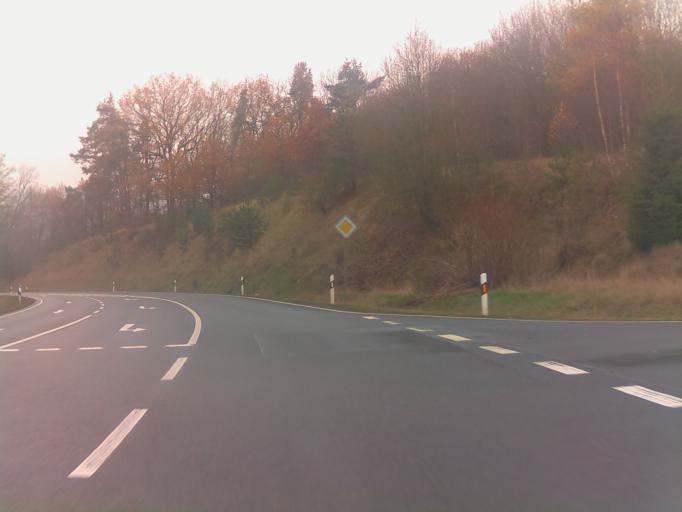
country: DE
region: Thuringia
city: Schleusingen
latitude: 50.5053
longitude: 10.7665
